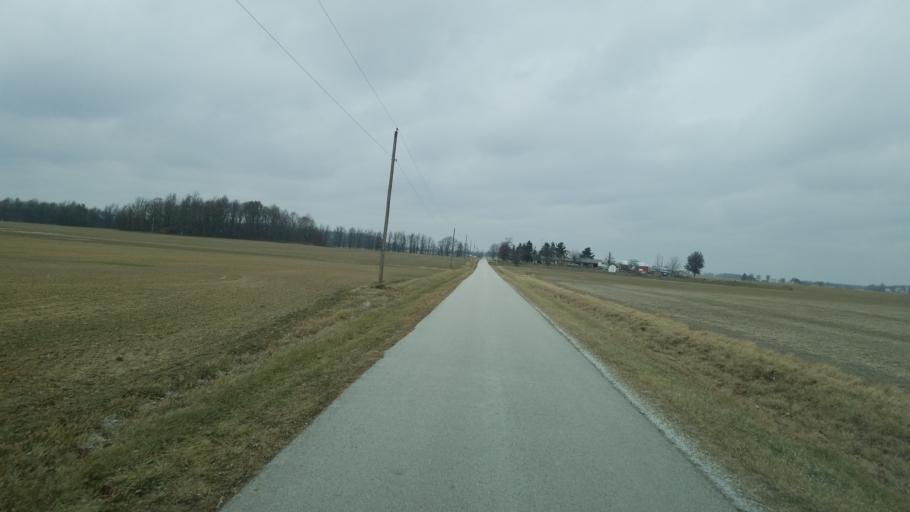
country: US
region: Ohio
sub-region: Hardin County
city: Forest
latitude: 40.7658
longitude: -83.4777
